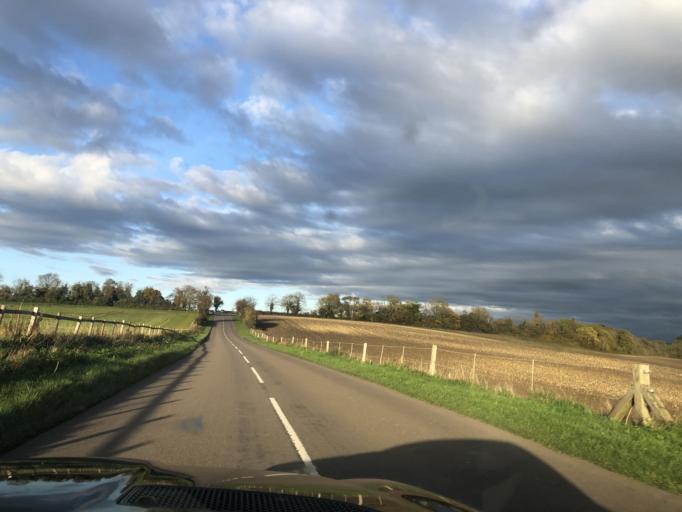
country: GB
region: England
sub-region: Warwickshire
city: Harbury
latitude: 52.2306
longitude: -1.4887
